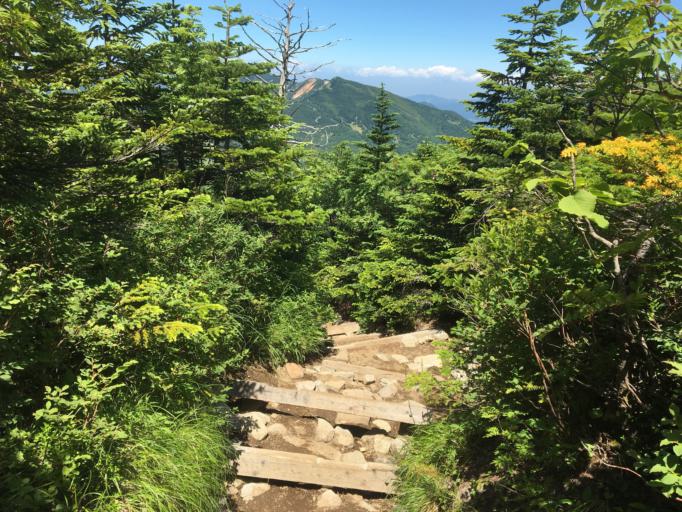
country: JP
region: Nagano
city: Komoro
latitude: 36.4010
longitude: 138.4867
